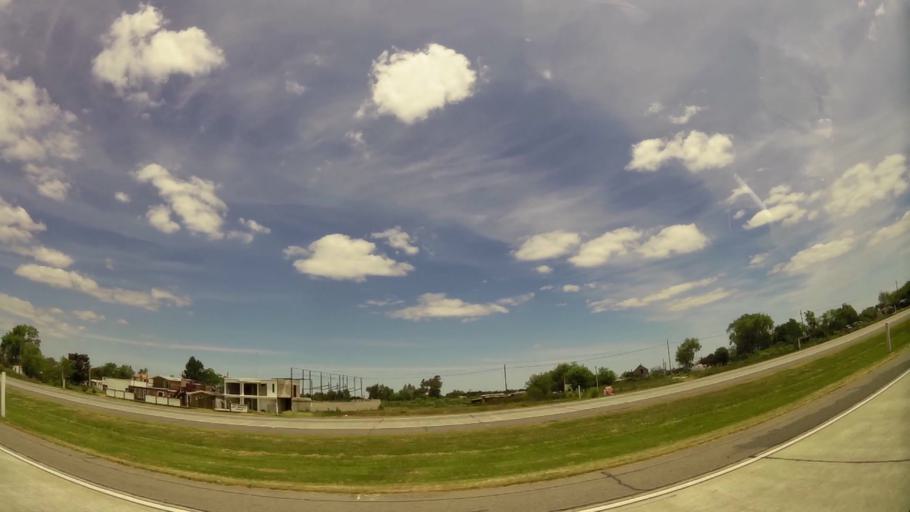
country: UY
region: San Jose
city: Delta del Tigre
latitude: -34.7632
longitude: -56.4100
